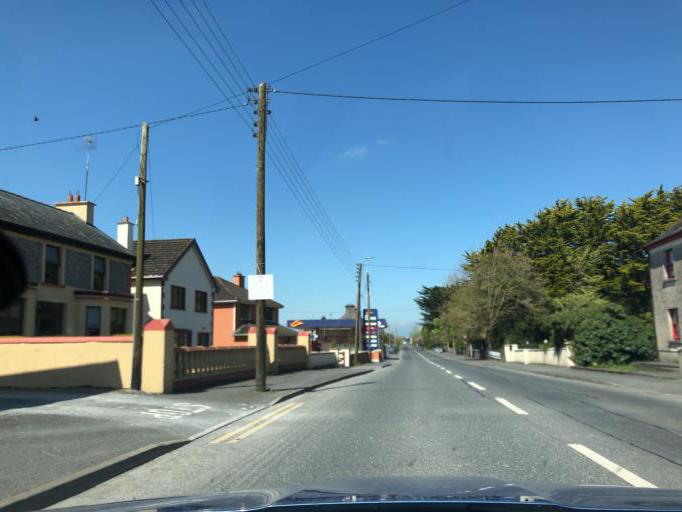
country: IE
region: Connaught
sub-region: County Galway
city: Athenry
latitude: 53.2304
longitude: -8.7352
